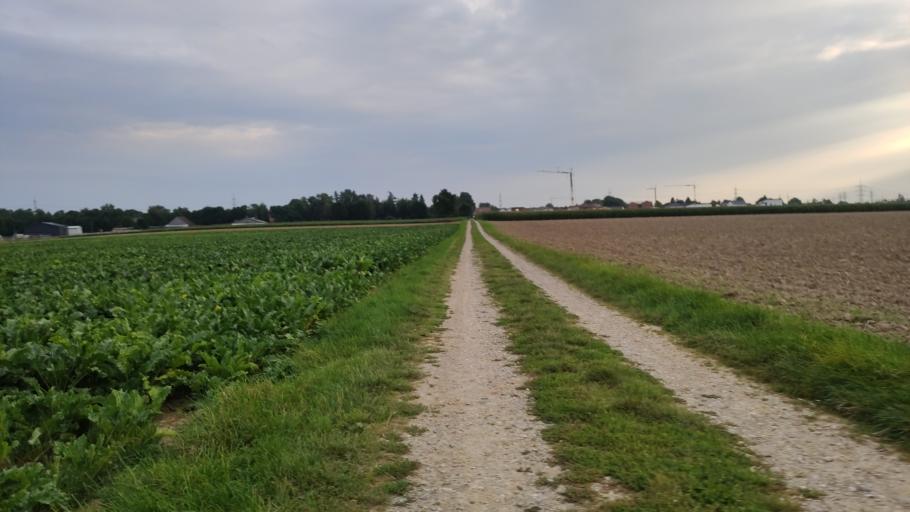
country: DE
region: Bavaria
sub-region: Swabia
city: Oberottmarshausen
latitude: 48.2443
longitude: 10.8593
